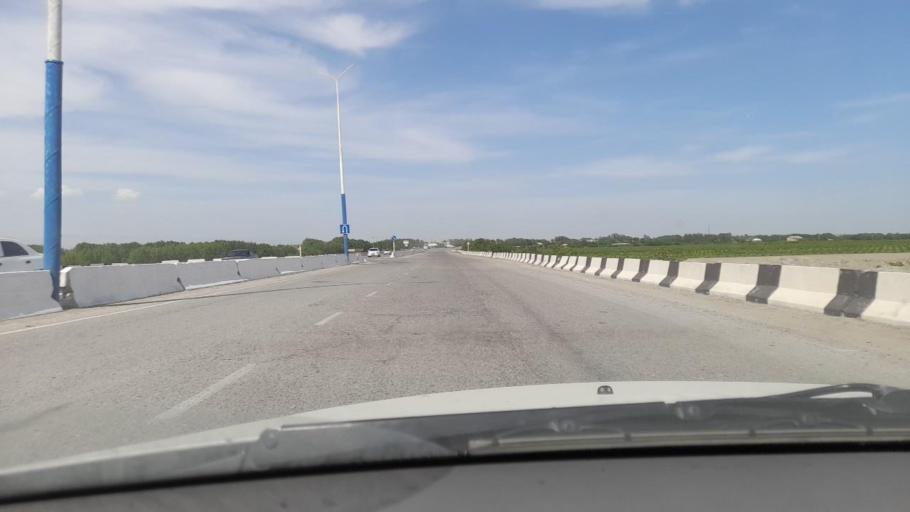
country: UZ
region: Samarqand
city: Kattaqo'rg'on
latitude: 39.9288
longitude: 66.3611
